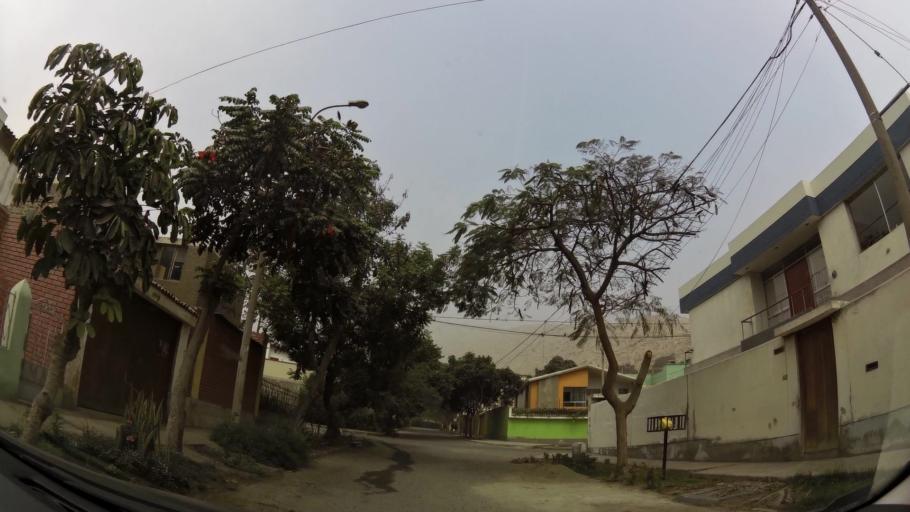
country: PE
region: Lima
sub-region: Lima
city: Chaclacayo
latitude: -11.9793
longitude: -76.7766
